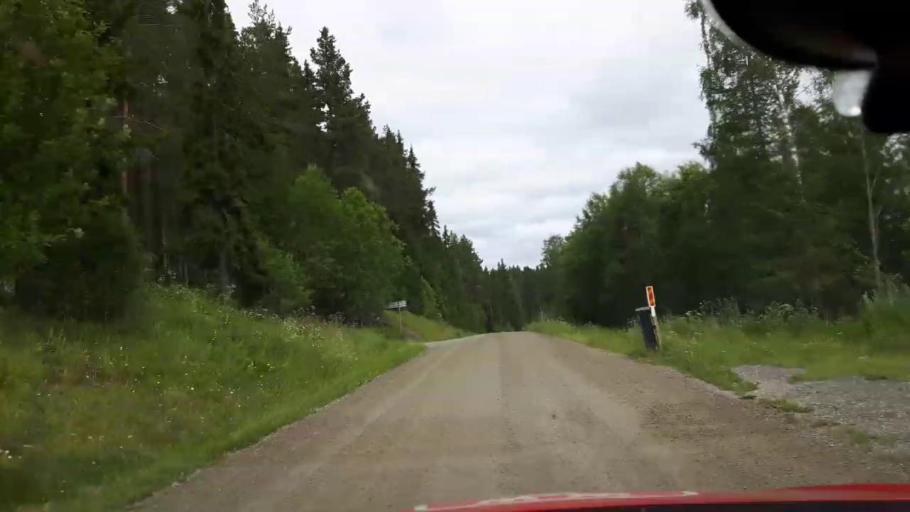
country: SE
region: Jaemtland
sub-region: OEstersunds Kommun
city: Brunflo
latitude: 62.9604
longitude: 15.0054
